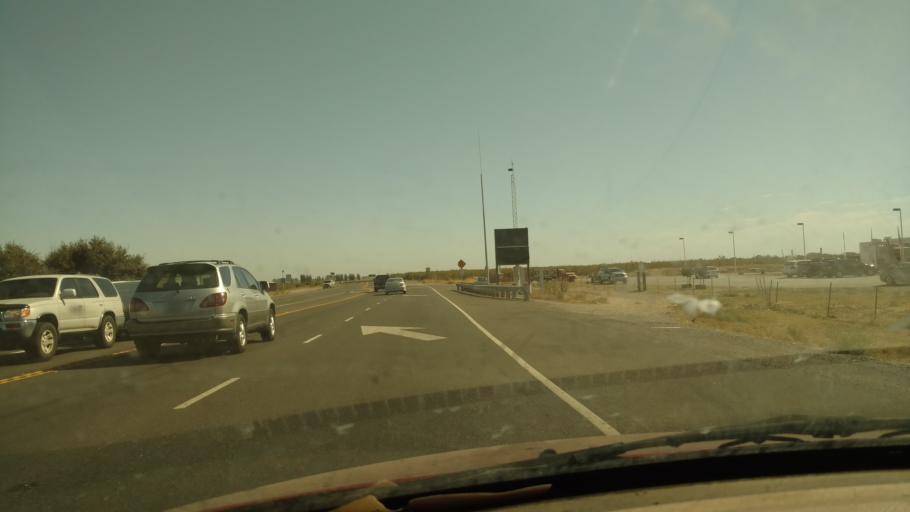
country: US
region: California
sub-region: Solano County
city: Rio Vista
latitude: 38.1549
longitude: -121.6760
